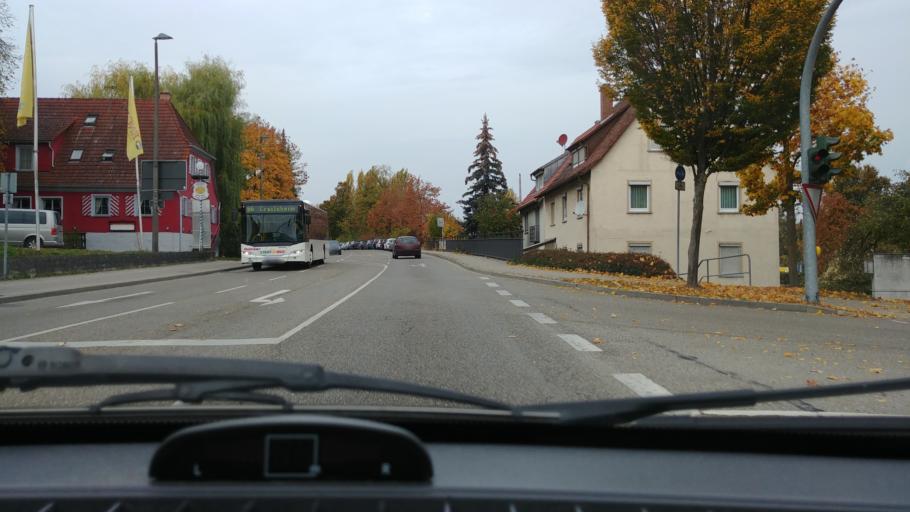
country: DE
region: Baden-Wuerttemberg
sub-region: Regierungsbezirk Stuttgart
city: Crailsheim
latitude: 49.1420
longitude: 10.0588
